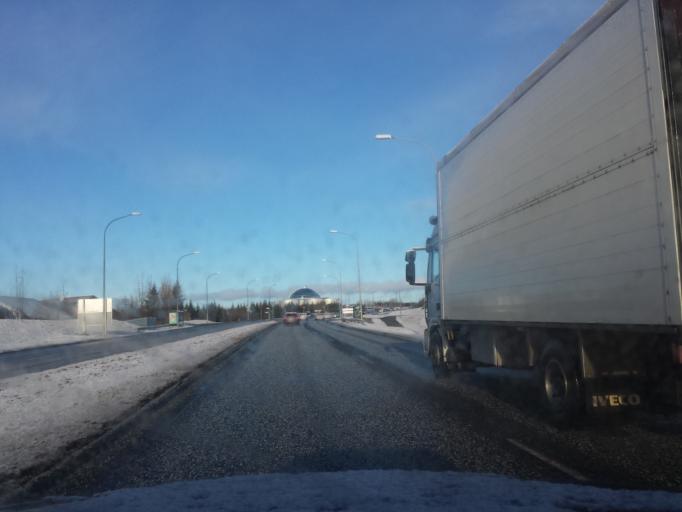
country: IS
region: Capital Region
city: Reykjavik
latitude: 64.1268
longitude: -21.9049
